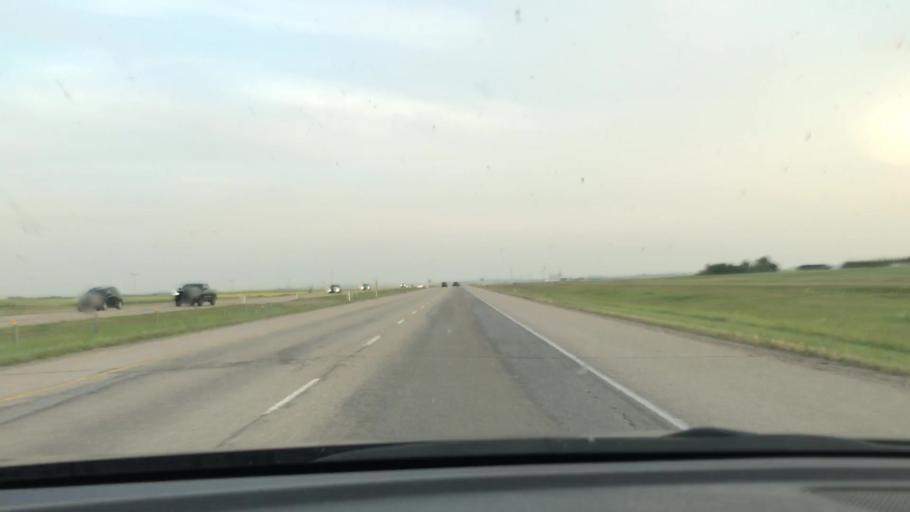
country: CA
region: Alberta
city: Carstairs
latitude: 51.5385
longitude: -114.0253
